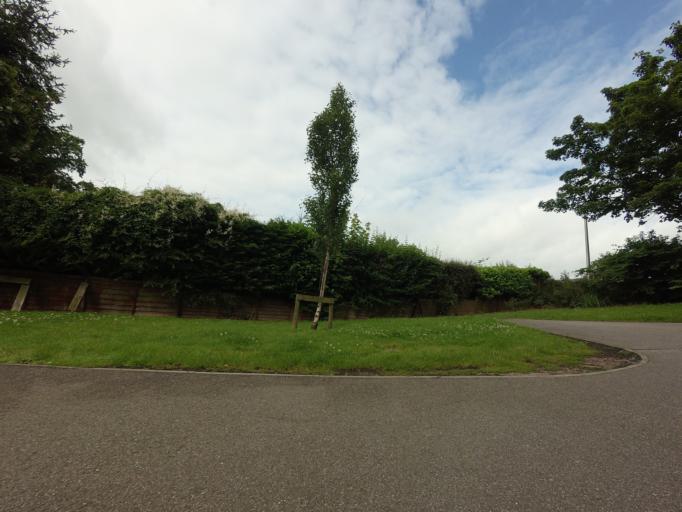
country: GB
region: Scotland
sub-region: Moray
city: Elgin
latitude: 57.6526
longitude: -3.3314
